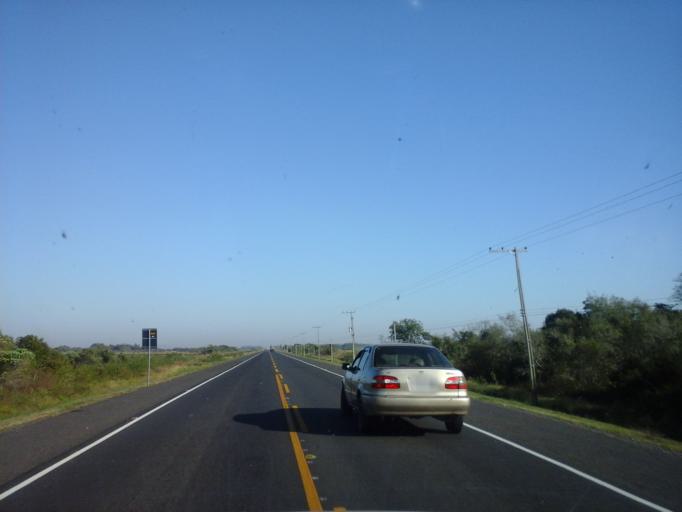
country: PY
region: Neembucu
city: Pilar
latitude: -26.8541
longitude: -58.2040
